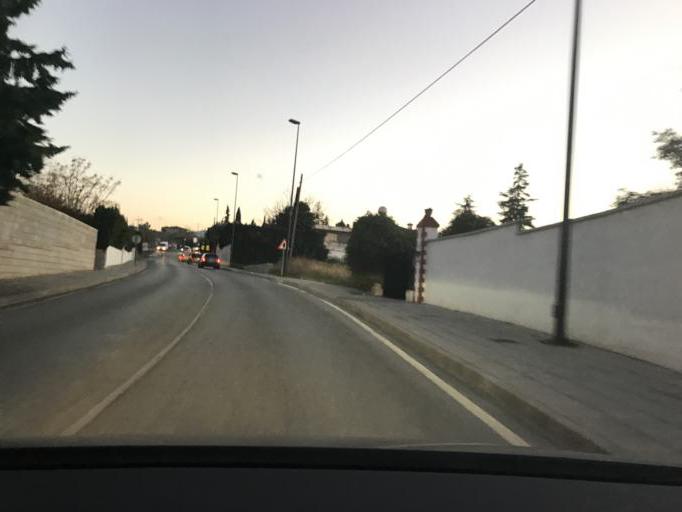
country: ES
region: Andalusia
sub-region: Provincia de Granada
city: Gojar
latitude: 37.1112
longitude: -3.6027
